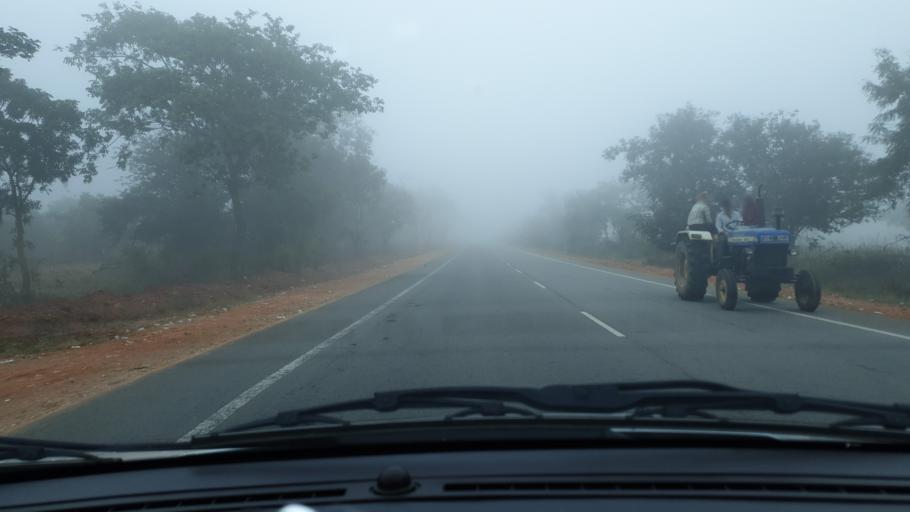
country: IN
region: Telangana
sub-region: Mahbubnagar
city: Nagar Karnul
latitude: 16.6460
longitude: 78.5838
